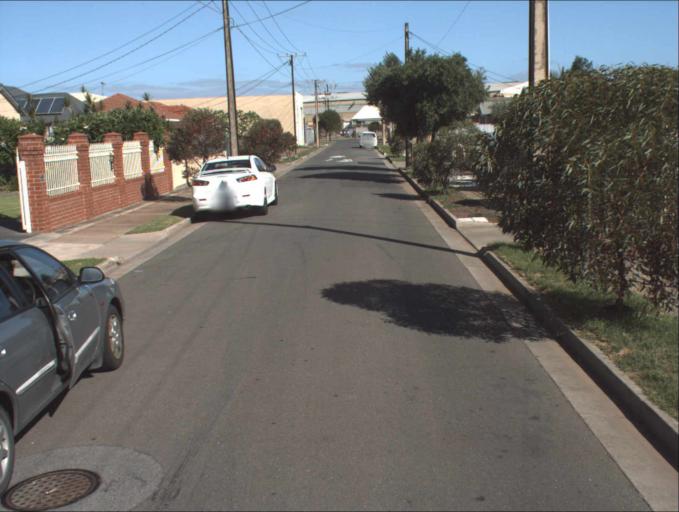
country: AU
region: South Australia
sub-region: Port Adelaide Enfield
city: Alberton
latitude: -34.8479
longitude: 138.5397
